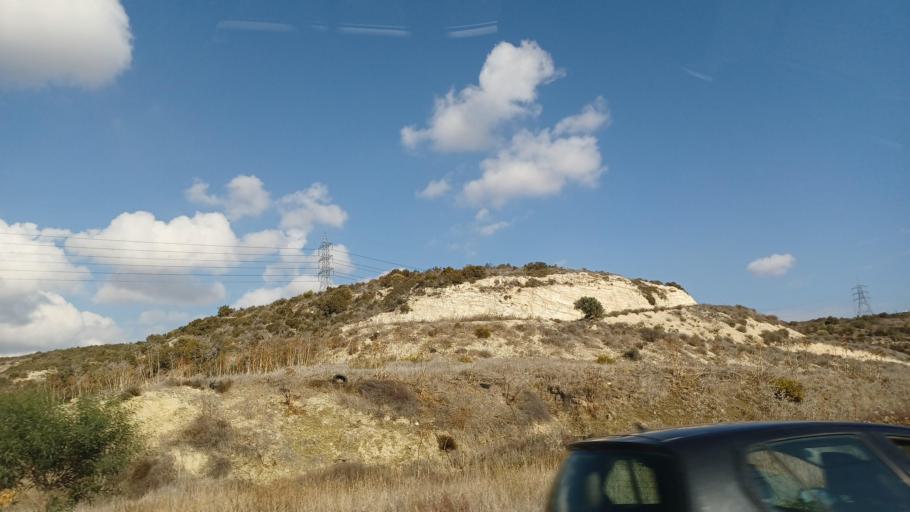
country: CY
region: Limassol
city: Pyrgos
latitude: 34.7231
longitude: 33.2553
